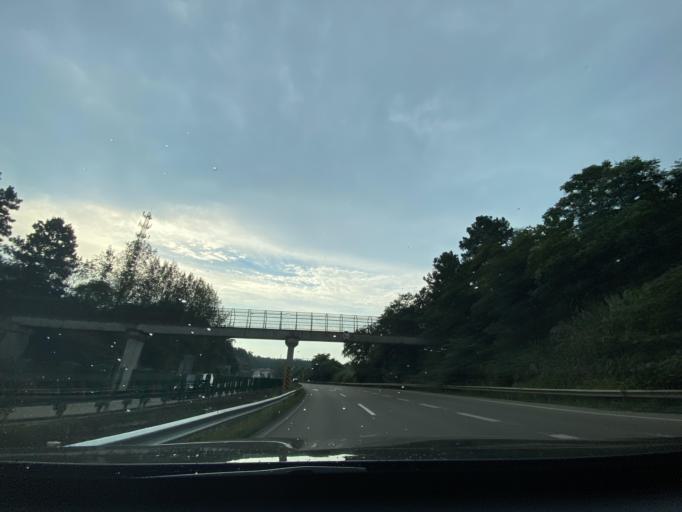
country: CN
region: Sichuan
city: Chonglong
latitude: 29.8072
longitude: 104.7088
